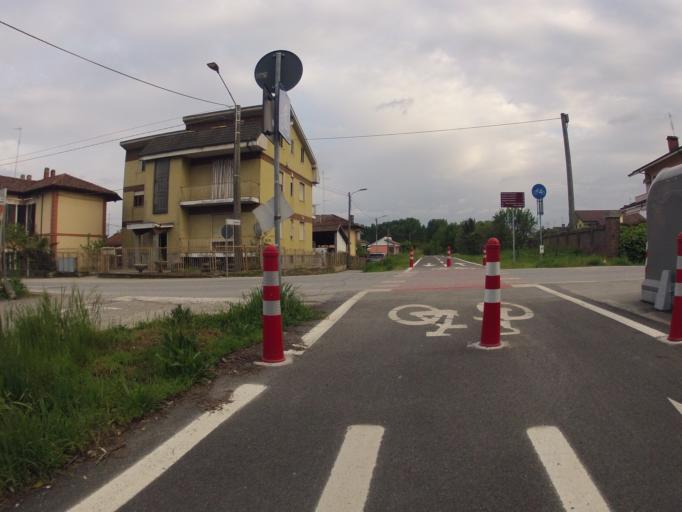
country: IT
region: Piedmont
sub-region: Provincia di Torino
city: Villafranca Piemonte
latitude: 44.7857
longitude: 7.5103
